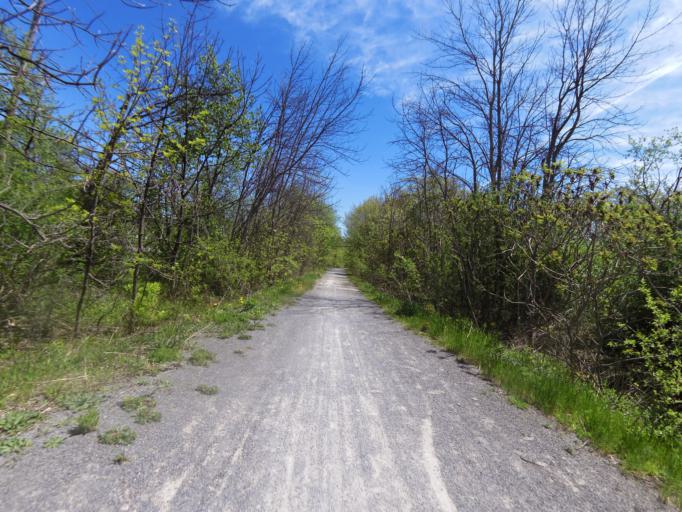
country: CA
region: Ontario
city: Bells Corners
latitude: 45.3851
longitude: -75.8114
